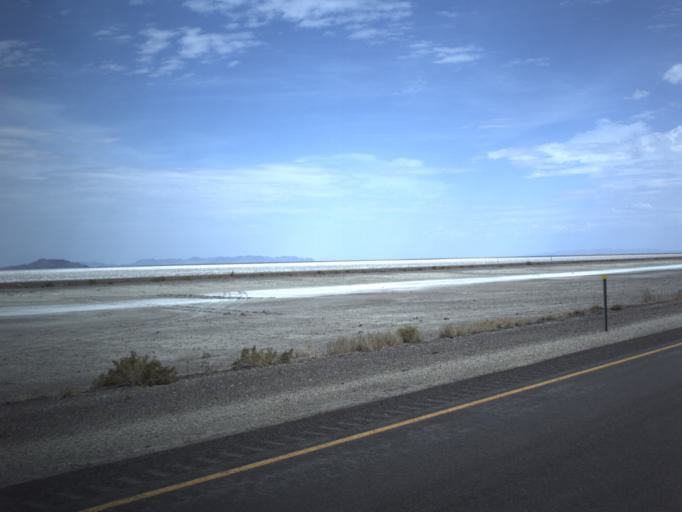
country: US
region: Utah
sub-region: Tooele County
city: Wendover
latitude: 40.7376
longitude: -113.8084
